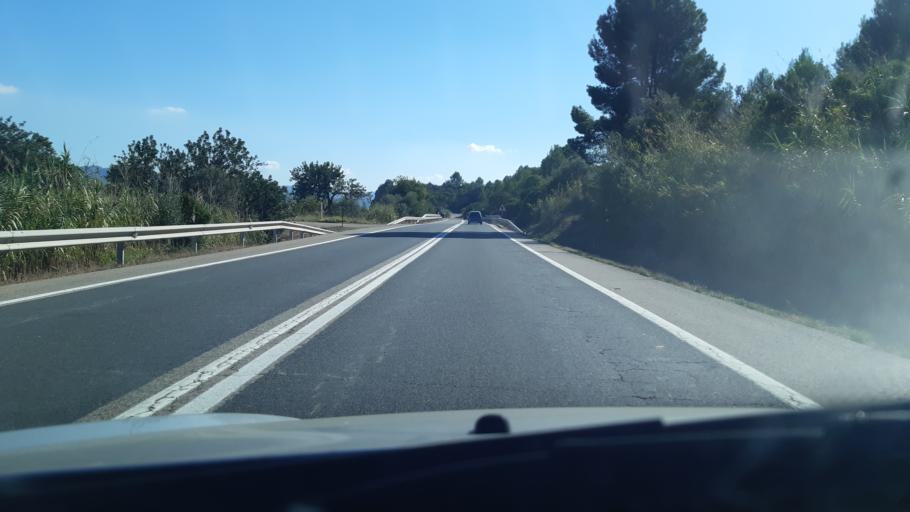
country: ES
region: Catalonia
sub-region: Provincia de Tarragona
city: Tivenys
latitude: 40.9010
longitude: 0.4833
